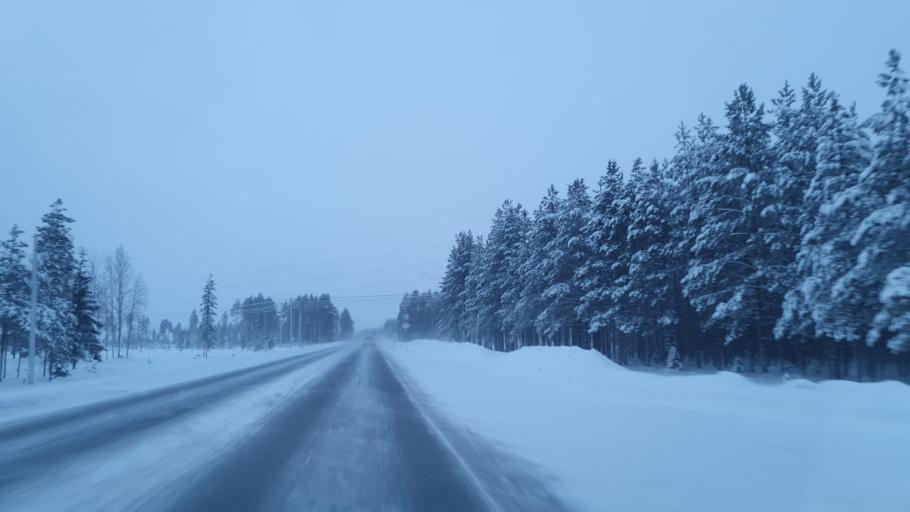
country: FI
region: Northern Ostrobothnia
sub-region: Oulunkaari
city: Utajaervi
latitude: 64.7351
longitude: 26.4716
